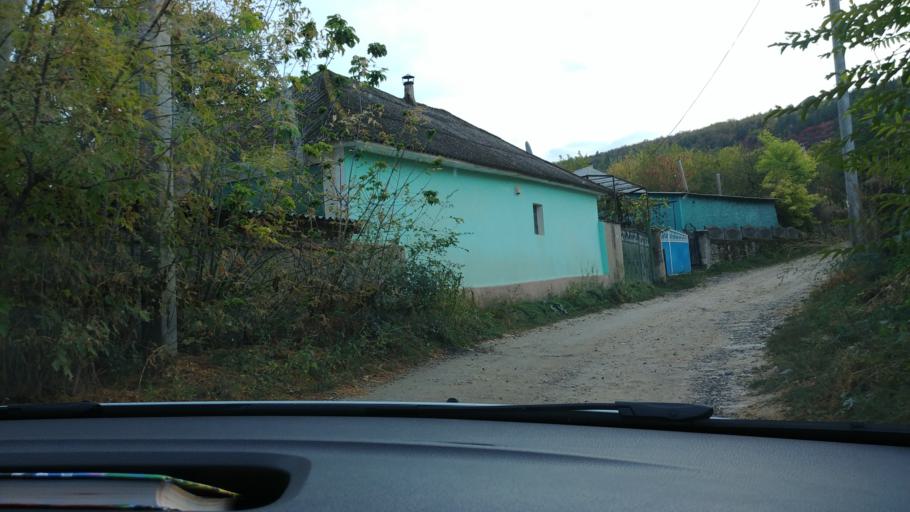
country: MD
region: Rezina
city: Saharna
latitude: 47.6897
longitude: 28.9763
